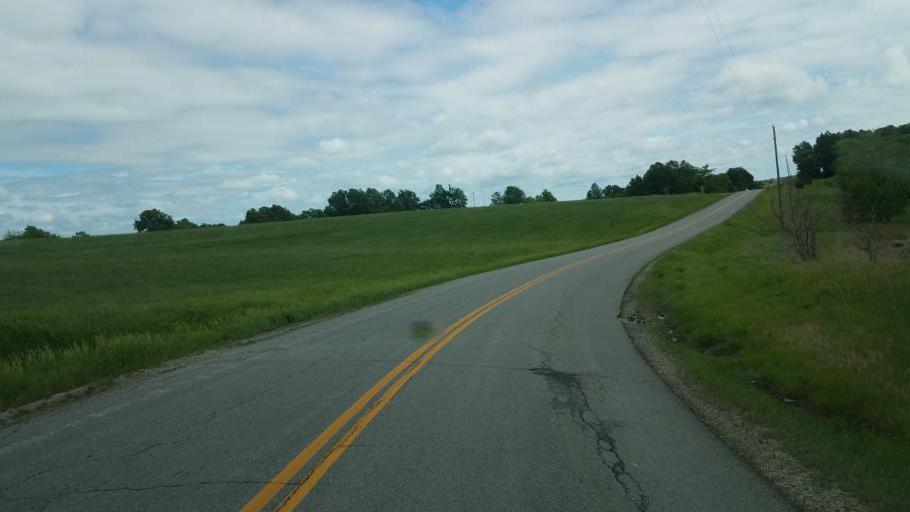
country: US
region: Iowa
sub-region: Decatur County
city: Lamoni
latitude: 40.4447
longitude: -93.8196
